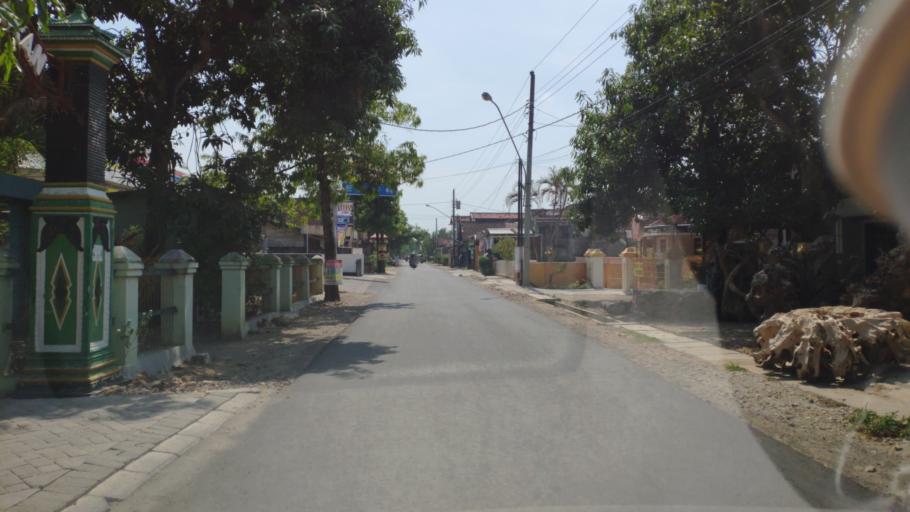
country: ID
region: Central Java
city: Mlangsen
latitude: -6.9789
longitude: 111.4160
